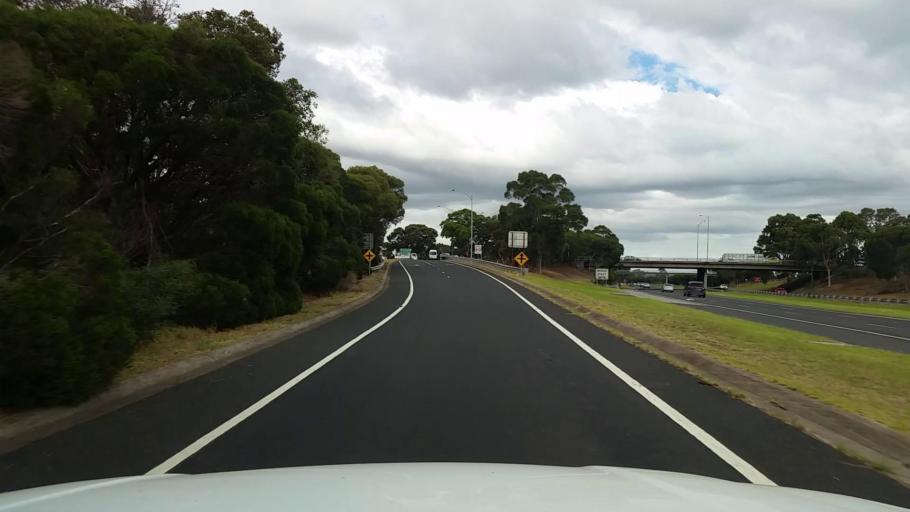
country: AU
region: Victoria
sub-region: Frankston
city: Seaford
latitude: -38.1069
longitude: 145.1399
